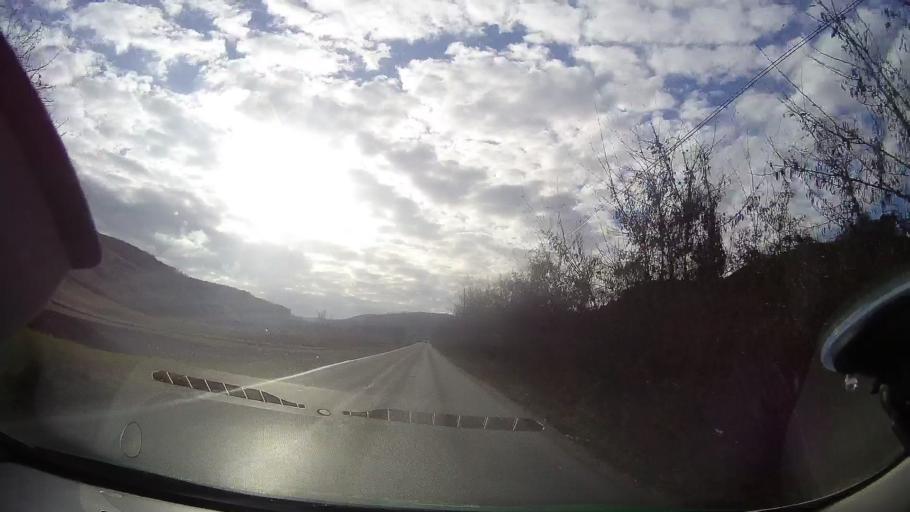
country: RO
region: Cluj
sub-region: Comuna Savadisla
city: Savadisla
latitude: 46.6823
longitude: 23.4562
